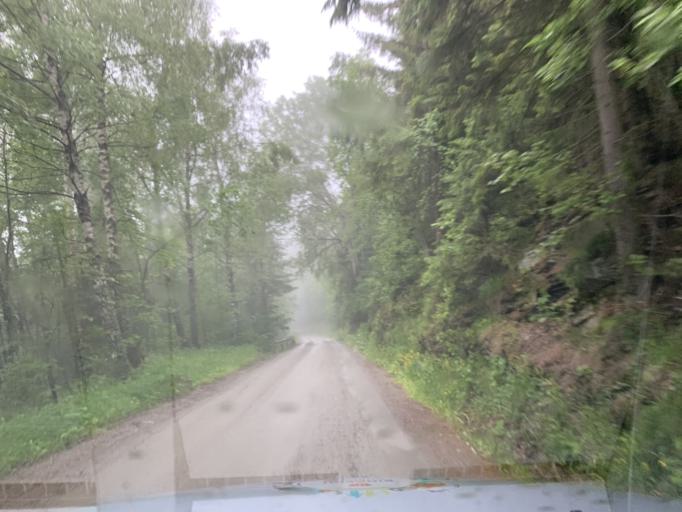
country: NO
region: Oppland
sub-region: Oyer
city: Tretten
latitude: 61.3908
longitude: 10.2602
